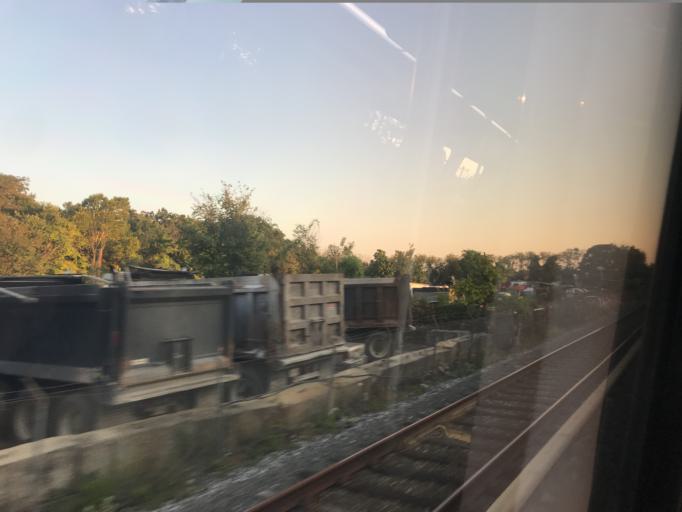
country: US
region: Maryland
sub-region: Prince George's County
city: Berwyn Heights
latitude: 38.9931
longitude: -76.9222
